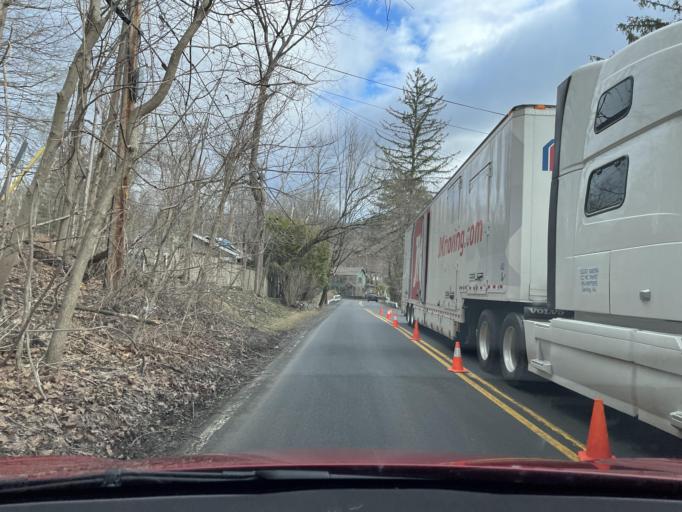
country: US
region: New York
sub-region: Ulster County
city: Woodstock
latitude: 42.0380
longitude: -74.1185
